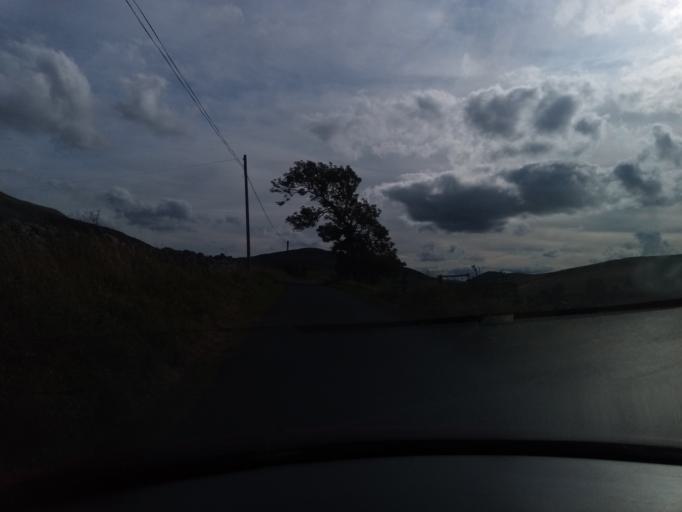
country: GB
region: Scotland
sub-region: The Scottish Borders
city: Kelso
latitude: 55.4756
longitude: -2.3529
